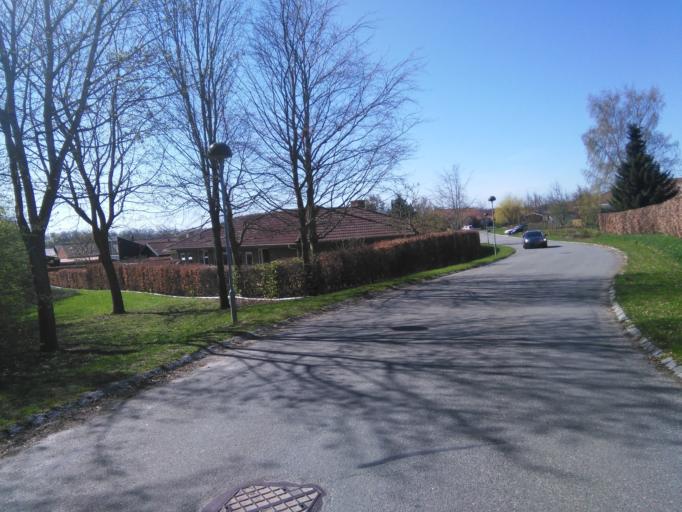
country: DK
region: Central Jutland
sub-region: Arhus Kommune
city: Marslet
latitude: 56.0692
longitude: 10.1739
